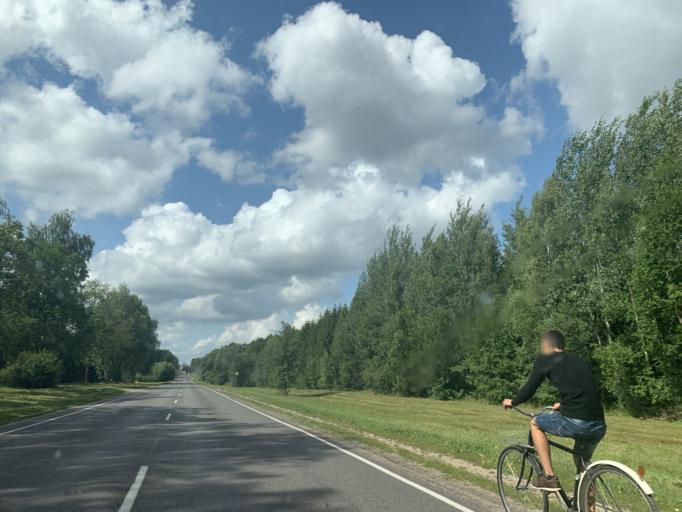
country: BY
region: Minsk
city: Enyerhyetykaw
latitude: 53.5763
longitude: 27.0590
